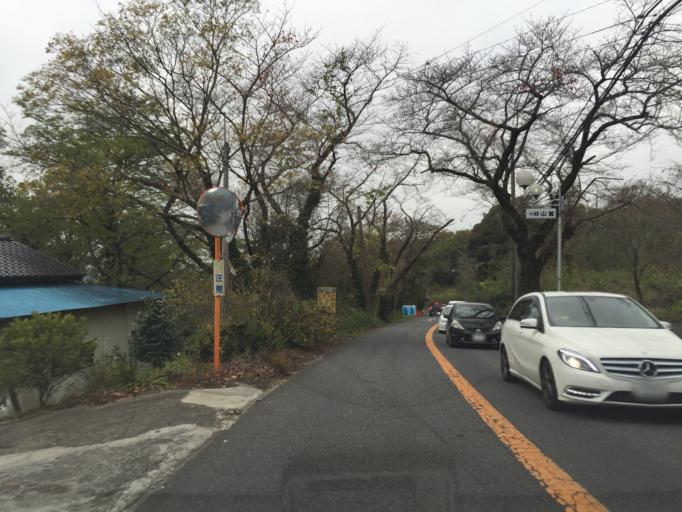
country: JP
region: Ibaraki
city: Tsukuba
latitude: 36.2099
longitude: 140.0880
